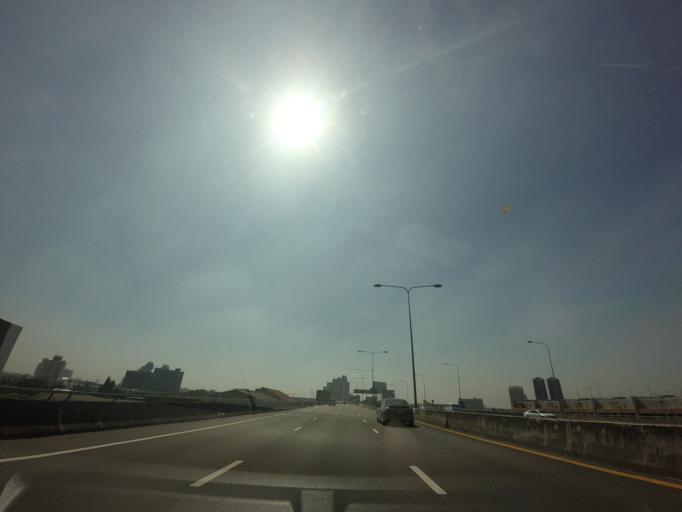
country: TH
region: Bangkok
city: Phra Khanong
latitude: 13.6838
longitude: 100.6027
